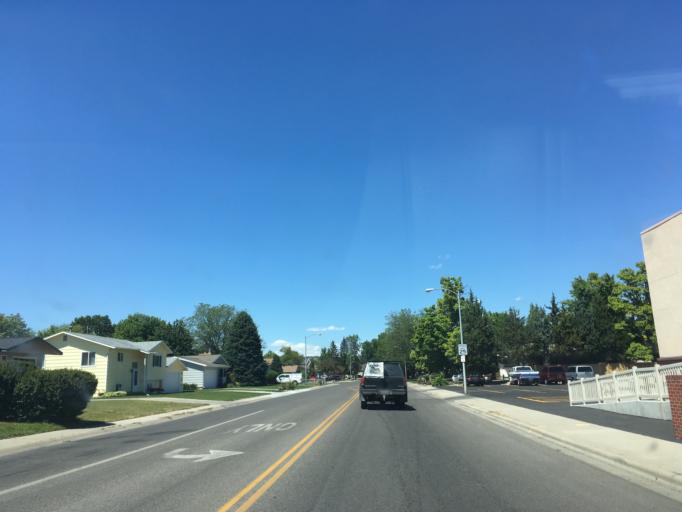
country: US
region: Montana
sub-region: Yellowstone County
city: Billings
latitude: 45.7700
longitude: -108.5647
